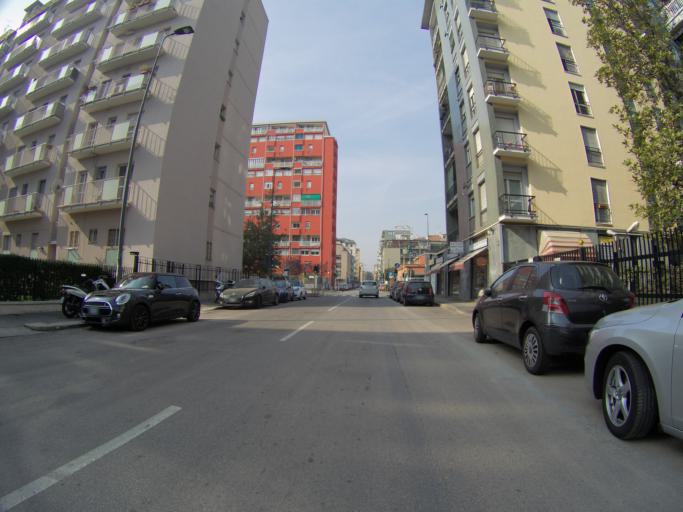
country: IT
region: Lombardy
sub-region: Citta metropolitana di Milano
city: Linate
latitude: 45.4656
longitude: 9.2333
